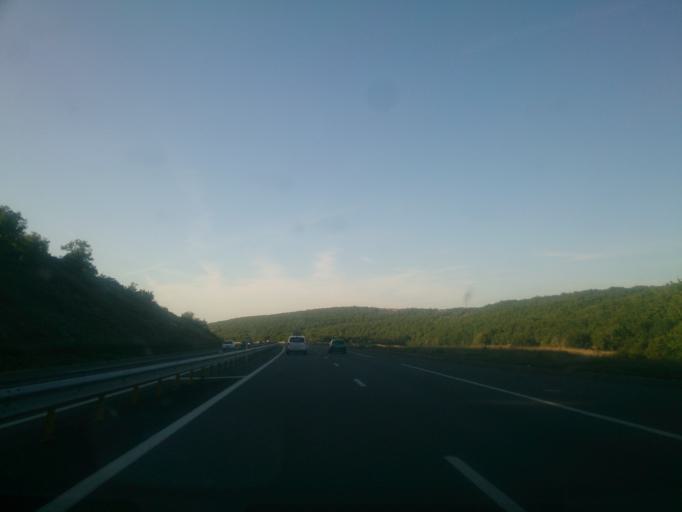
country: FR
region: Midi-Pyrenees
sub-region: Departement du Lot
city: Le Vigan
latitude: 44.7653
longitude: 1.5399
